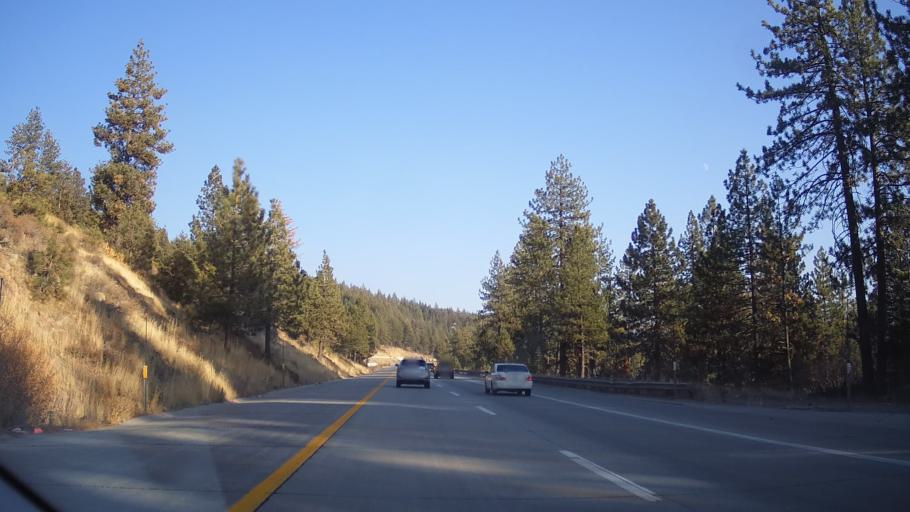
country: US
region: California
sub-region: Nevada County
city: Truckee
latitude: 39.3313
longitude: -120.2531
